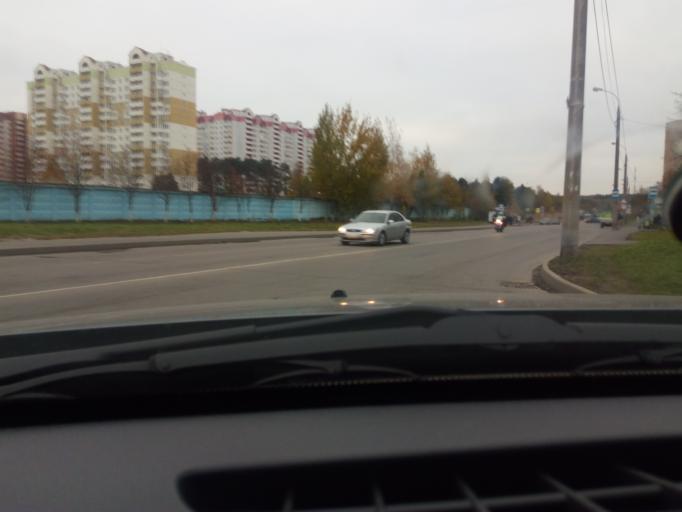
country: RU
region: Moskovskaya
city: Reutov
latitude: 55.7436
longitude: 37.8804
